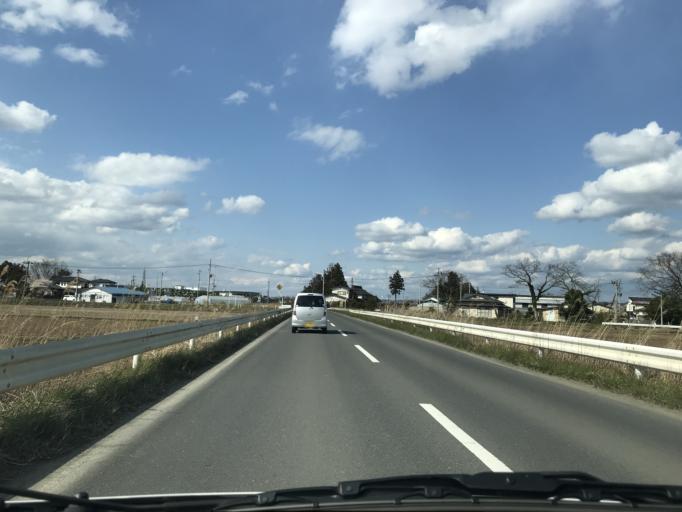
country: JP
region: Miyagi
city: Wakuya
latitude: 38.6927
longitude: 141.2338
